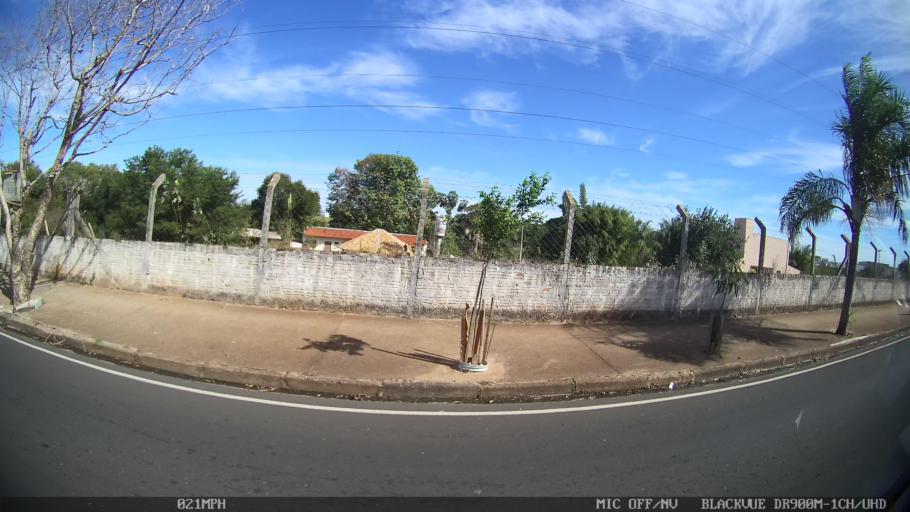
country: BR
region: Sao Paulo
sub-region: Sao Jose Do Rio Preto
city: Sao Jose do Rio Preto
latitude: -20.8481
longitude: -49.3685
